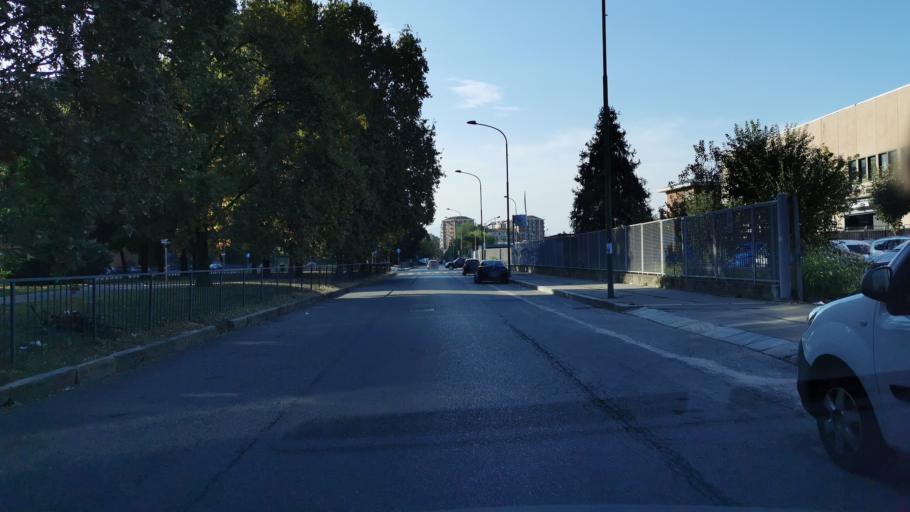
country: IT
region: Piedmont
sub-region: Provincia di Torino
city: Turin
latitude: 45.0980
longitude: 7.7079
